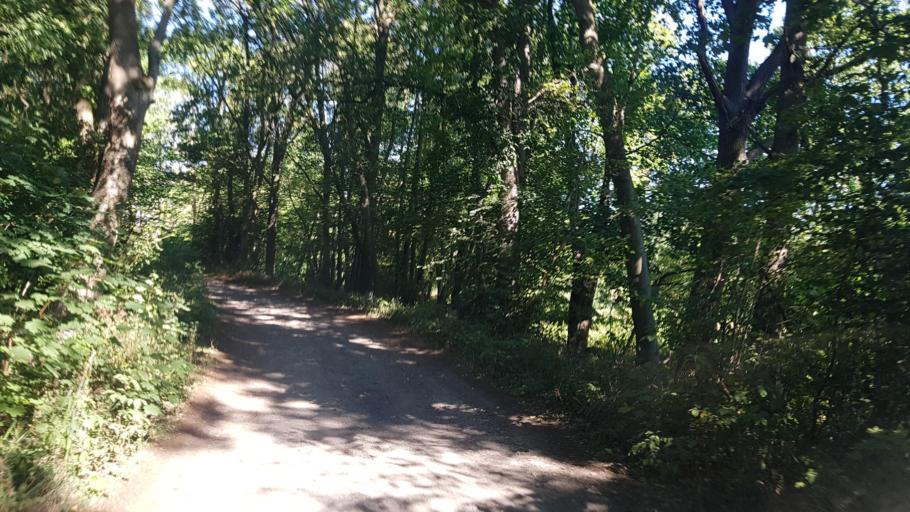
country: DE
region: Brandenburg
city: Brandenburg an der Havel
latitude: 52.3444
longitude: 12.5318
